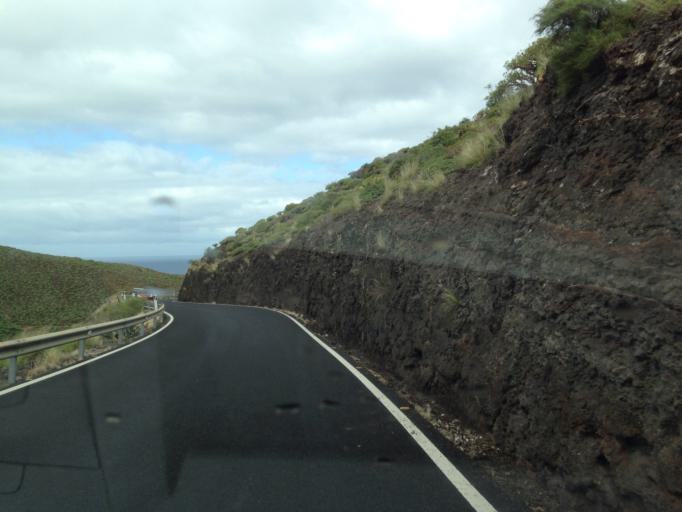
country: ES
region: Canary Islands
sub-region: Provincia de Las Palmas
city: Agaete
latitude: 28.0940
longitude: -15.7014
